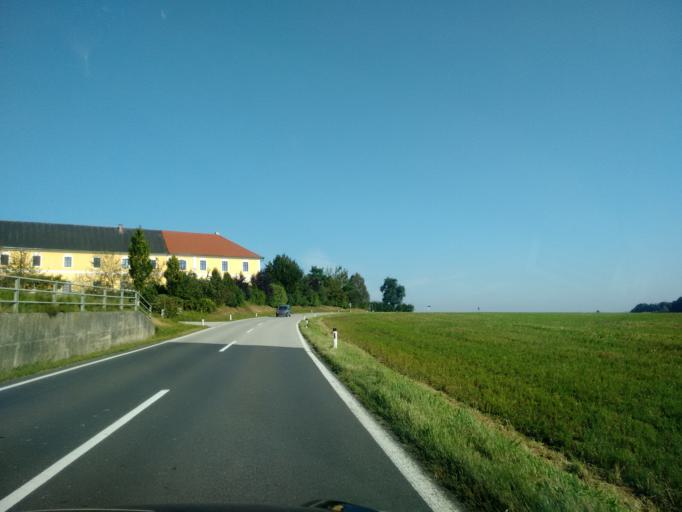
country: AT
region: Upper Austria
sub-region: Politischer Bezirk Steyr-Land
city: Bad Hall
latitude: 48.0789
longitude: 14.1904
